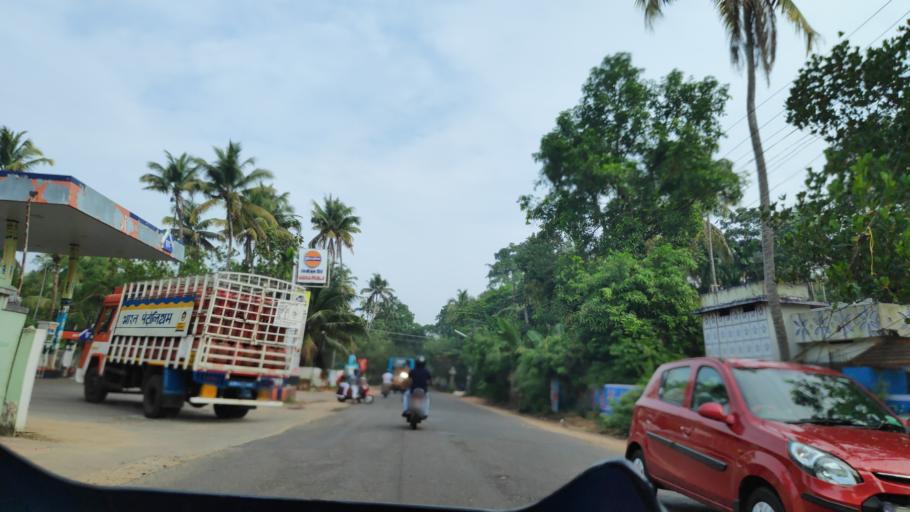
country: IN
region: Kerala
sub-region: Alappuzha
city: Shertallai
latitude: 9.7091
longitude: 76.3576
